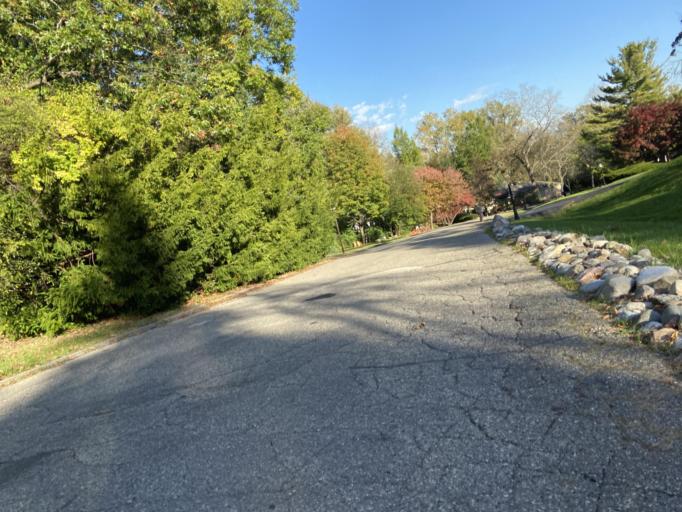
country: US
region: Michigan
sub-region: Oakland County
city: Franklin
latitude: 42.5056
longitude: -83.3285
